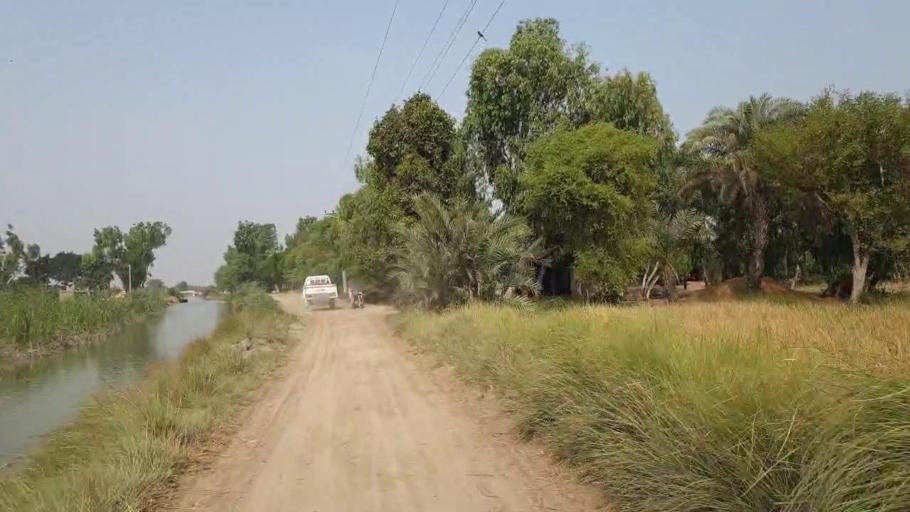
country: PK
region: Sindh
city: Kario
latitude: 24.8339
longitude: 68.5443
